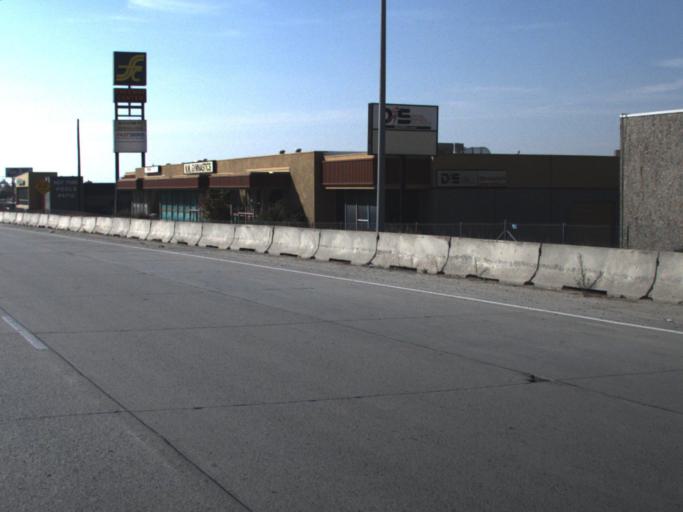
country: US
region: Washington
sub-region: Spokane County
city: Spokane Valley
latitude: 47.6740
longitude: -117.2464
